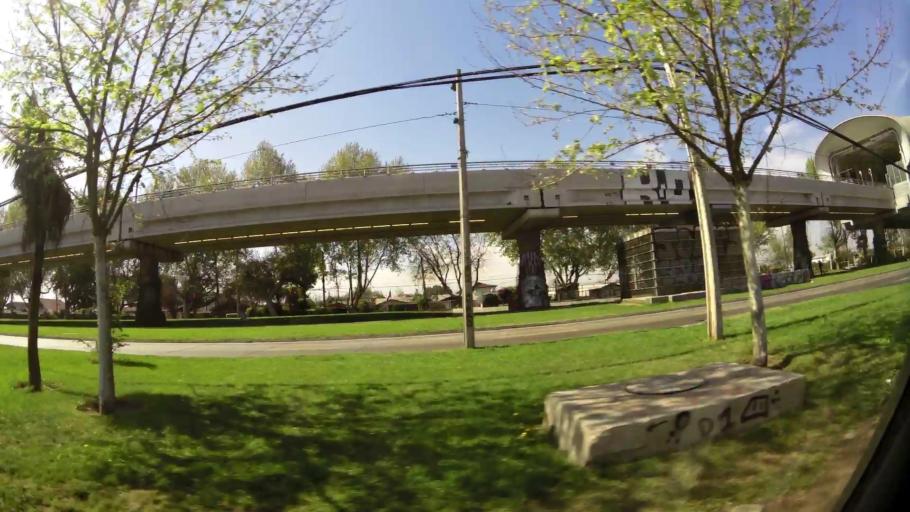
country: CL
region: Santiago Metropolitan
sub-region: Provincia de Santiago
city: Lo Prado
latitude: -33.4744
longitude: -70.7397
